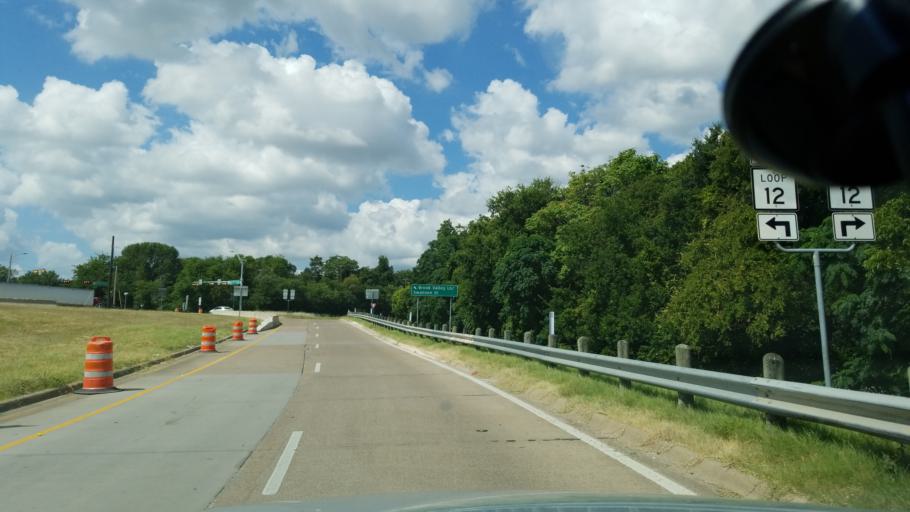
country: US
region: Texas
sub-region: Dallas County
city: Cockrell Hill
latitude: 32.6923
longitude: -96.8472
